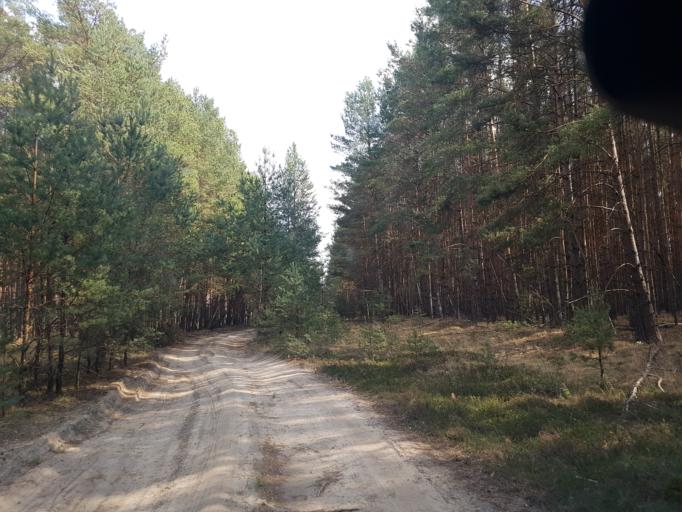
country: DE
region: Brandenburg
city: Treuenbrietzen
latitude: 52.0310
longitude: 12.8832
